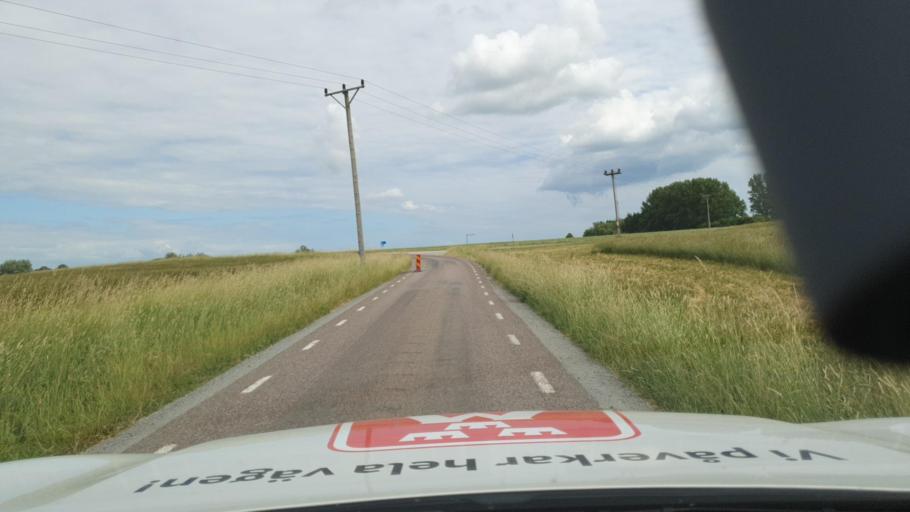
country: SE
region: Skane
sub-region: Trelleborgs Kommun
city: Anderslov
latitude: 55.4742
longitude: 13.3556
